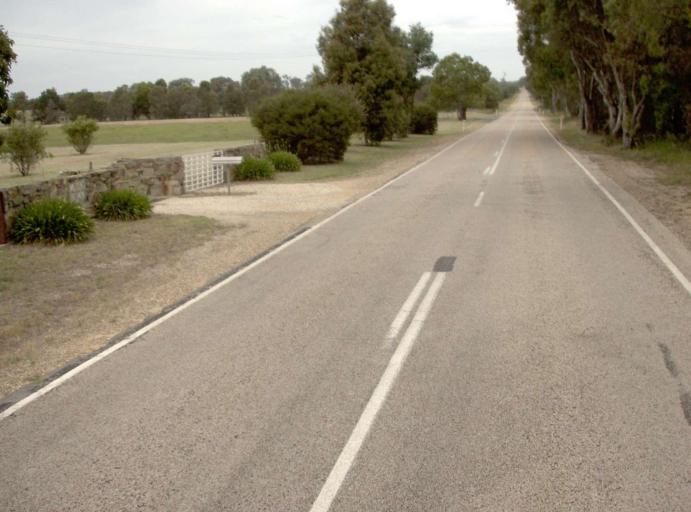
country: AU
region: Victoria
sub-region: East Gippsland
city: Bairnsdale
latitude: -37.8702
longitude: 147.4249
